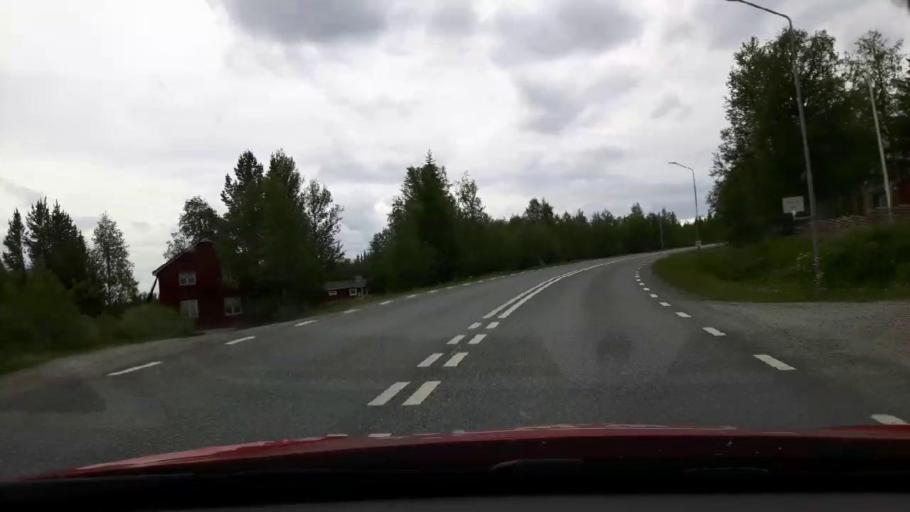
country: NO
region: Hedmark
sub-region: Engerdal
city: Engerdal
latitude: 62.5428
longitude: 12.4691
